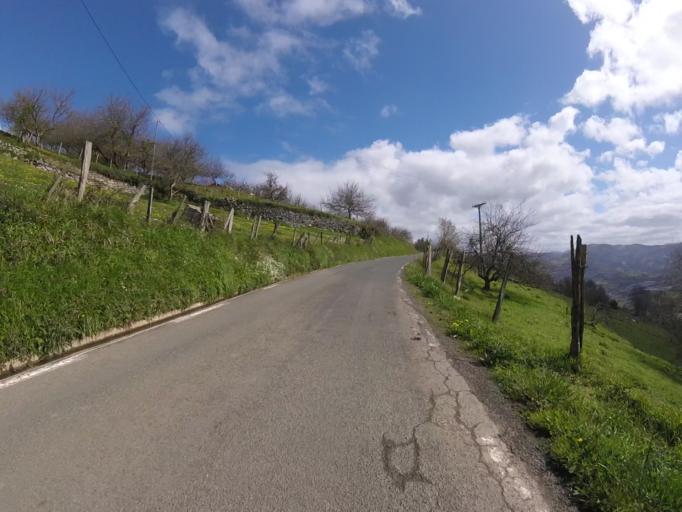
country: ES
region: Basque Country
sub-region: Provincia de Guipuzcoa
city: Tolosa
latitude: 43.1321
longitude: -2.1058
